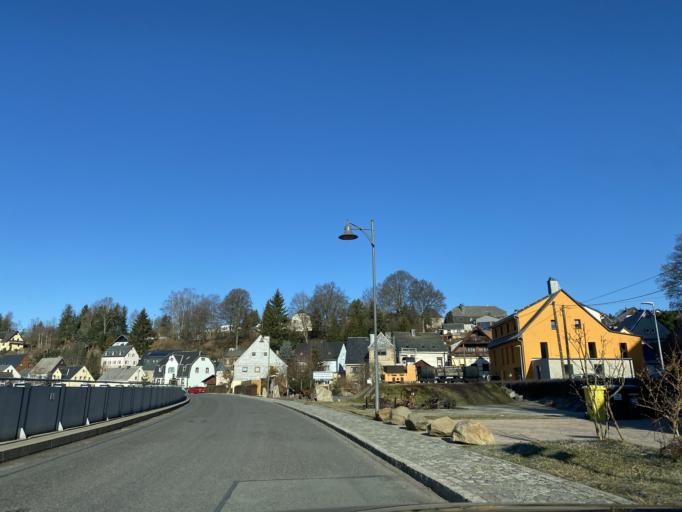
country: DE
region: Saxony
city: Wiesa
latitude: 50.6111
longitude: 13.0191
